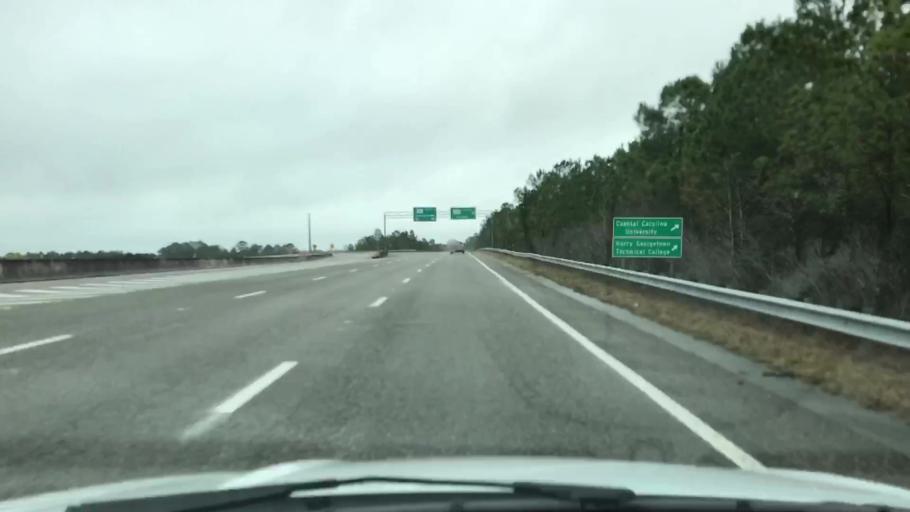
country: US
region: South Carolina
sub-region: Horry County
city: Forestbrook
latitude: 33.7414
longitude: -78.9484
